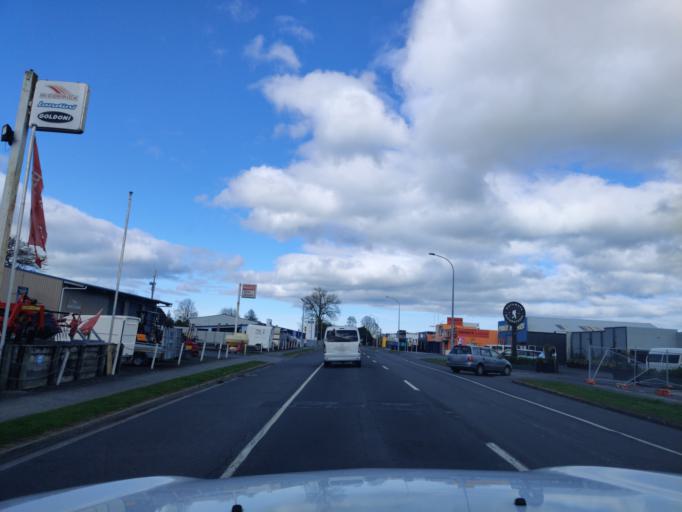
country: NZ
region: Waikato
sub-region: Matamata-Piako District
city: Matamata
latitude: -37.8106
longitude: 175.7706
